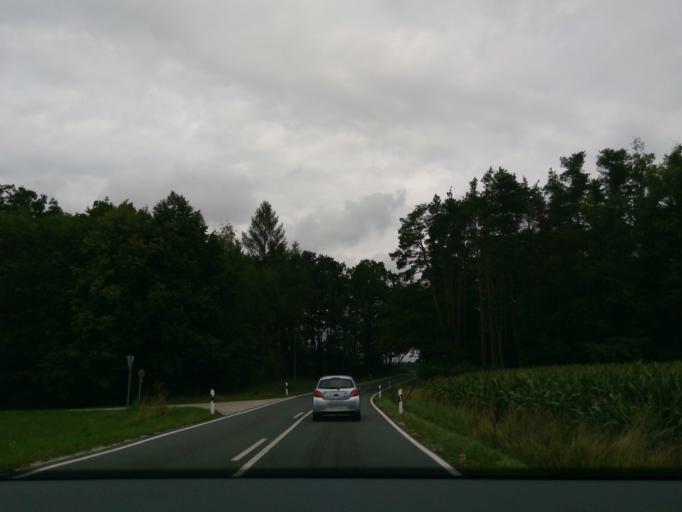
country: DE
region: Bavaria
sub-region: Regierungsbezirk Mittelfranken
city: Weisendorf
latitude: 49.6443
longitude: 10.8169
